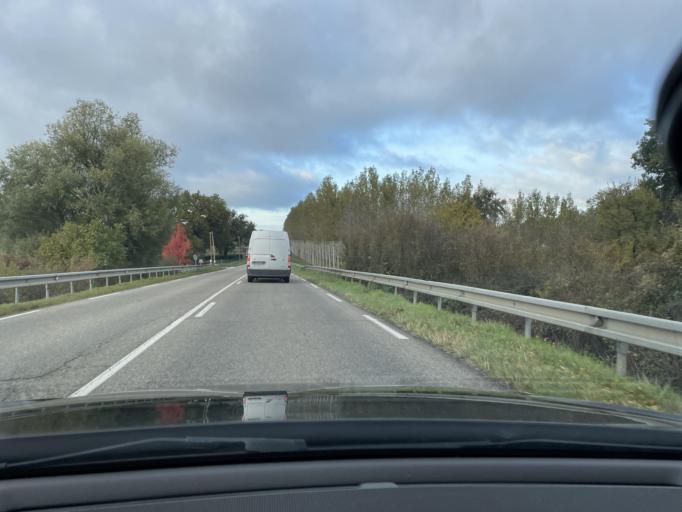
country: FR
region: Aquitaine
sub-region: Departement du Lot-et-Garonne
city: Casteljaloux
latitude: 44.3619
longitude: 0.1071
